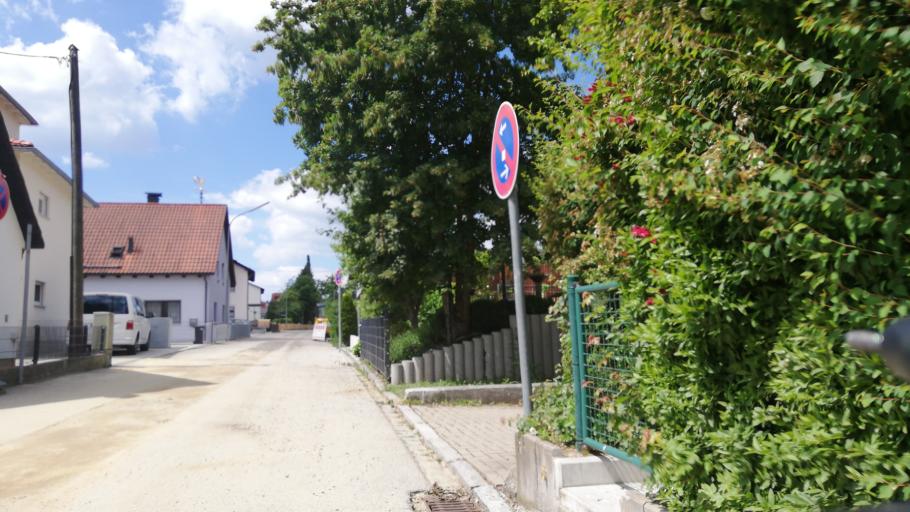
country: DE
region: Bavaria
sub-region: Upper Bavaria
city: Pfaffenhofen an der Ilm
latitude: 48.5316
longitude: 11.4974
